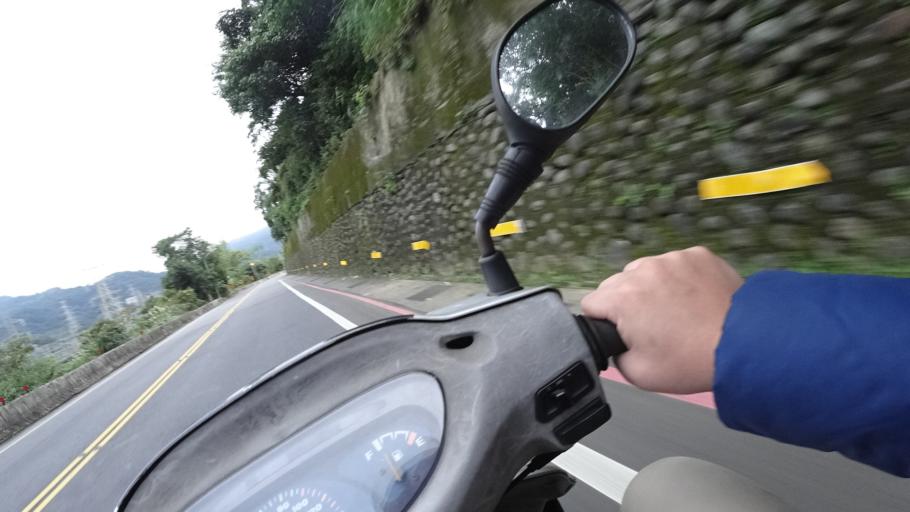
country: TW
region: Taipei
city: Taipei
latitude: 25.0066
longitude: 121.6253
